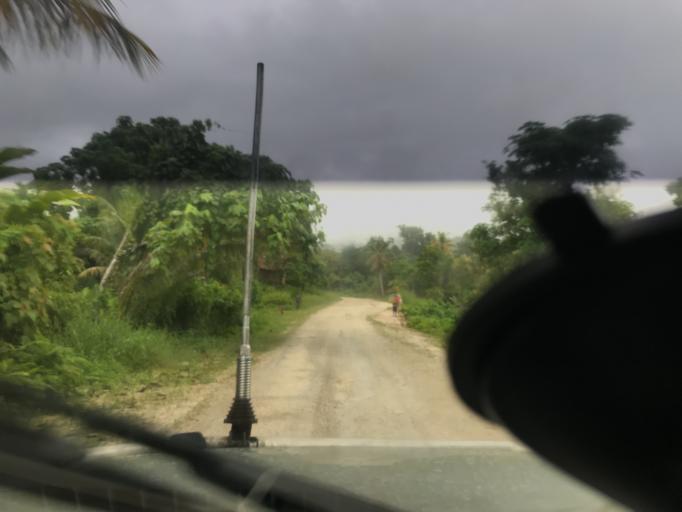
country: SB
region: Malaita
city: Auki
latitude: -9.0218
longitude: 160.8029
